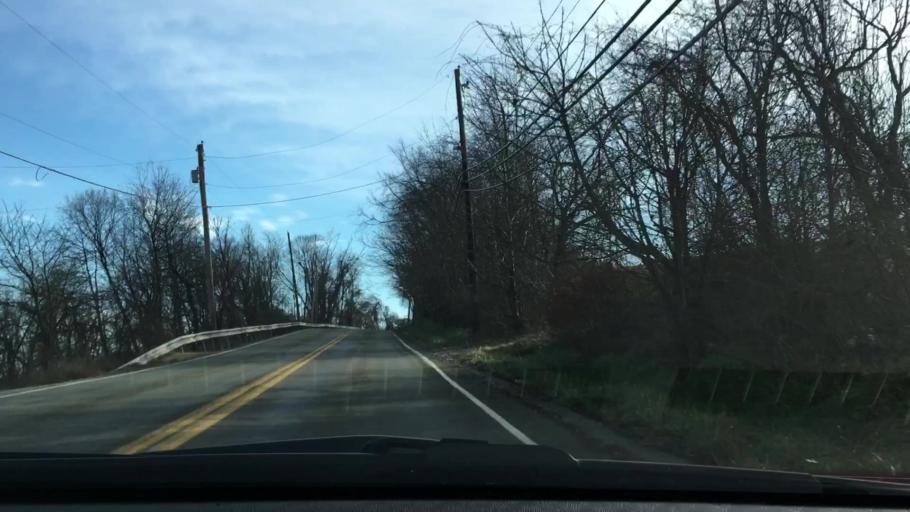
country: US
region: Pennsylvania
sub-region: Westmoreland County
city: West Newton
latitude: 40.2050
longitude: -79.7506
